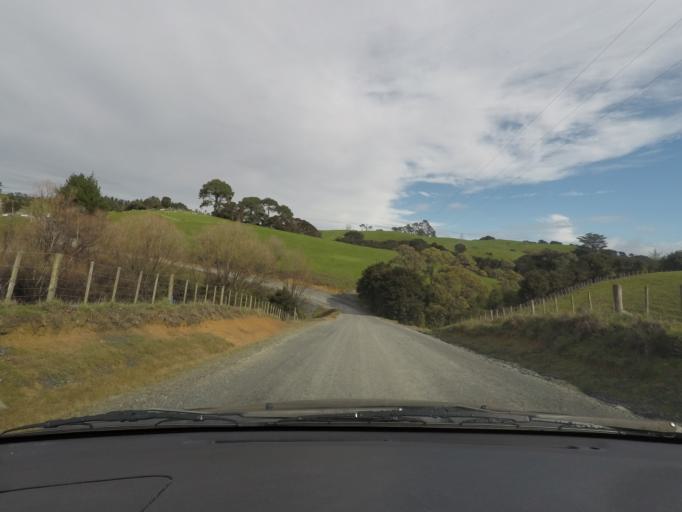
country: NZ
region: Auckland
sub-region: Auckland
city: Warkworth
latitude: -36.4488
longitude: 174.7502
